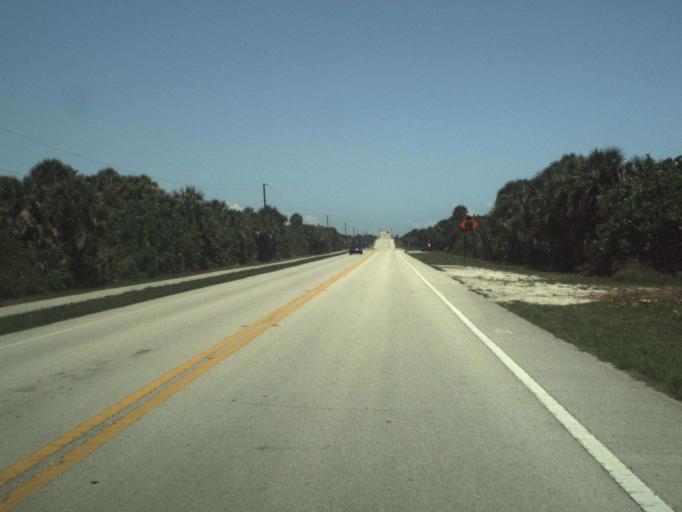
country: US
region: Florida
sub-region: Indian River County
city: Sebastian
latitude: 27.8529
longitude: -80.4447
